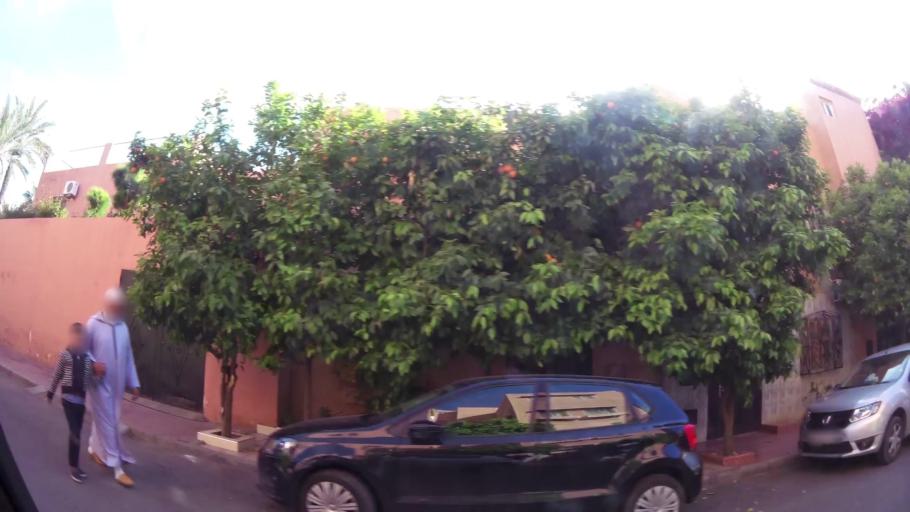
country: MA
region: Marrakech-Tensift-Al Haouz
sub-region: Marrakech
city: Marrakesh
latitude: 31.6594
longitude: -8.0109
